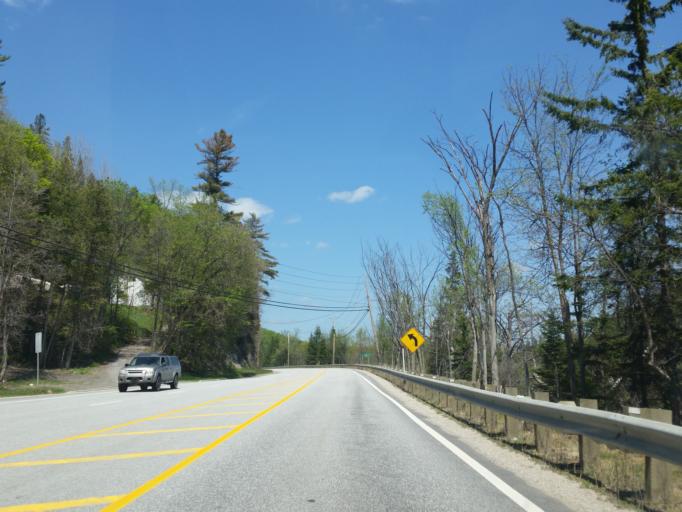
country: CA
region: Quebec
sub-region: Outaouais
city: Wakefield
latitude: 45.6740
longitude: -75.9290
